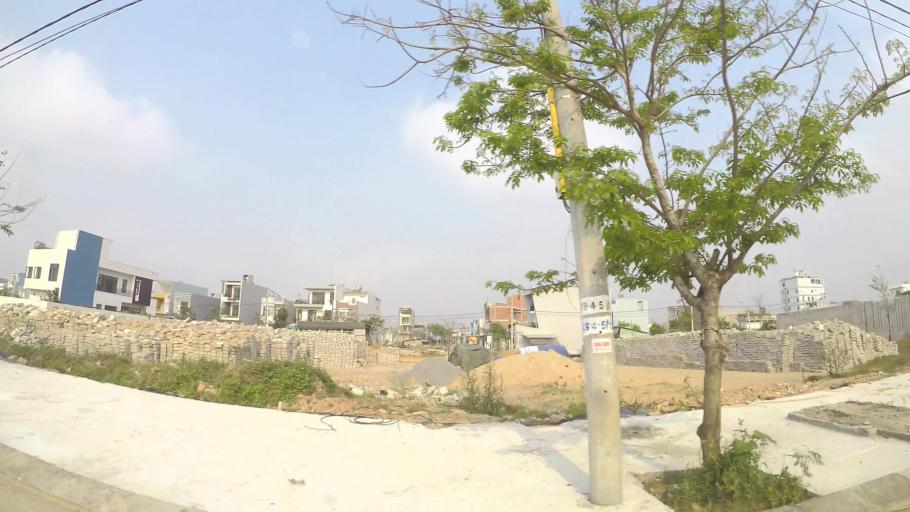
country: VN
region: Da Nang
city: Ngu Hanh Son
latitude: 16.0076
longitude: 108.2304
